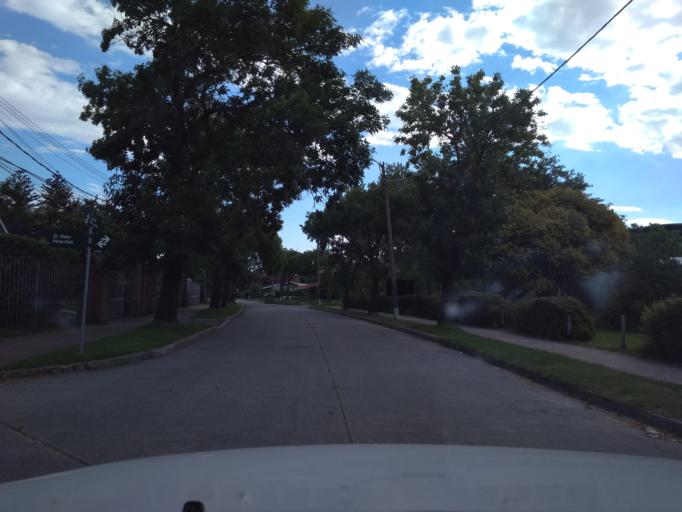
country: UY
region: Canelones
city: Paso de Carrasco
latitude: -34.8868
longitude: -56.0838
